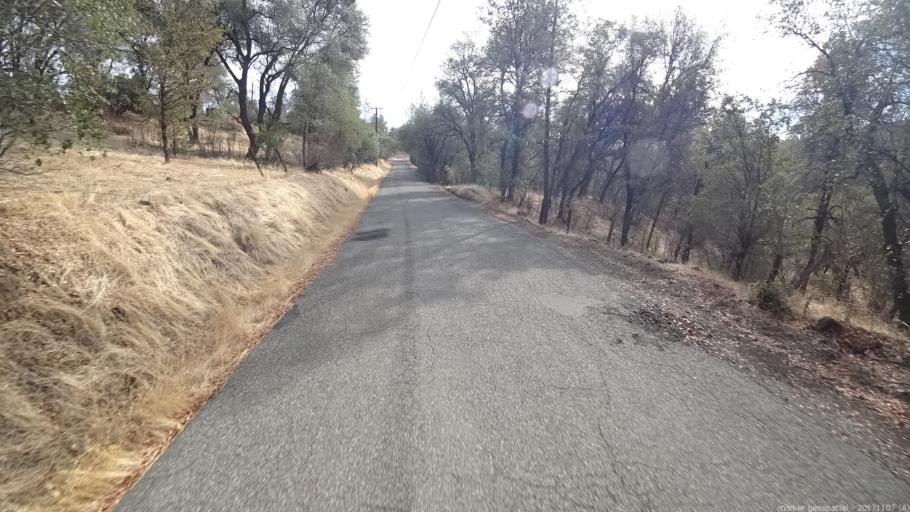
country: US
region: California
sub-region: Shasta County
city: Shasta
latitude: 40.5230
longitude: -122.5538
